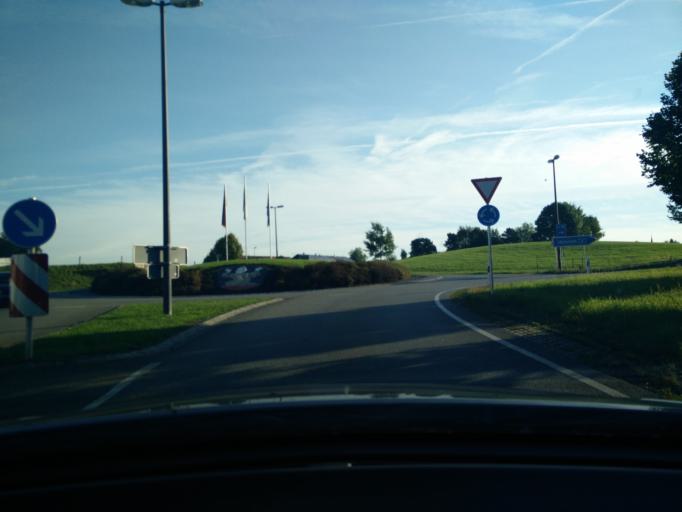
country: DE
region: Bavaria
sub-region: Upper Bavaria
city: Irschenberg
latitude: 47.8313
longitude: 11.9061
